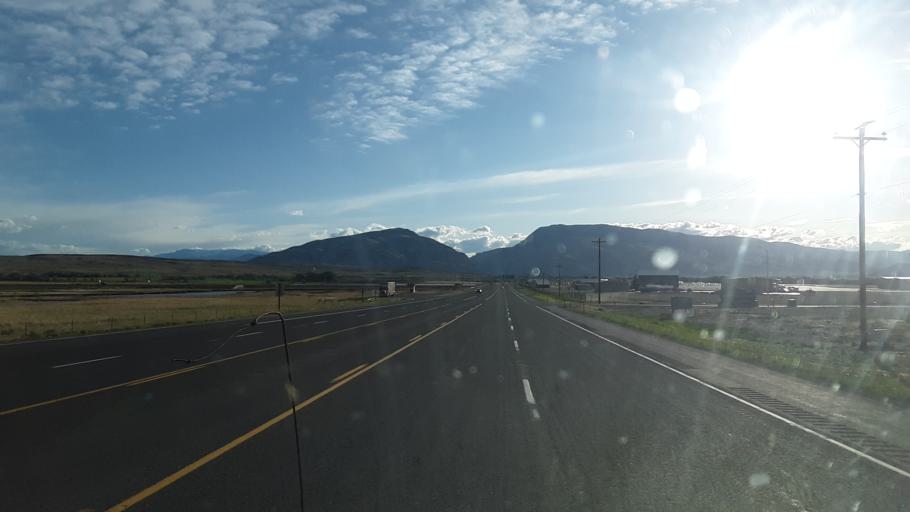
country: US
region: Wyoming
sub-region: Park County
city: Cody
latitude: 44.5117
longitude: -109.0176
